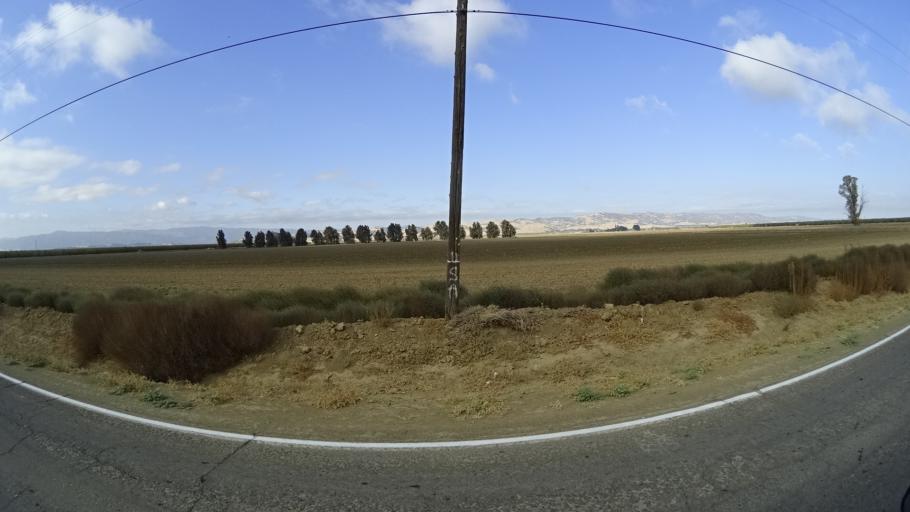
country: US
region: California
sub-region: Yolo County
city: Esparto
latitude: 38.7469
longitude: -122.0073
